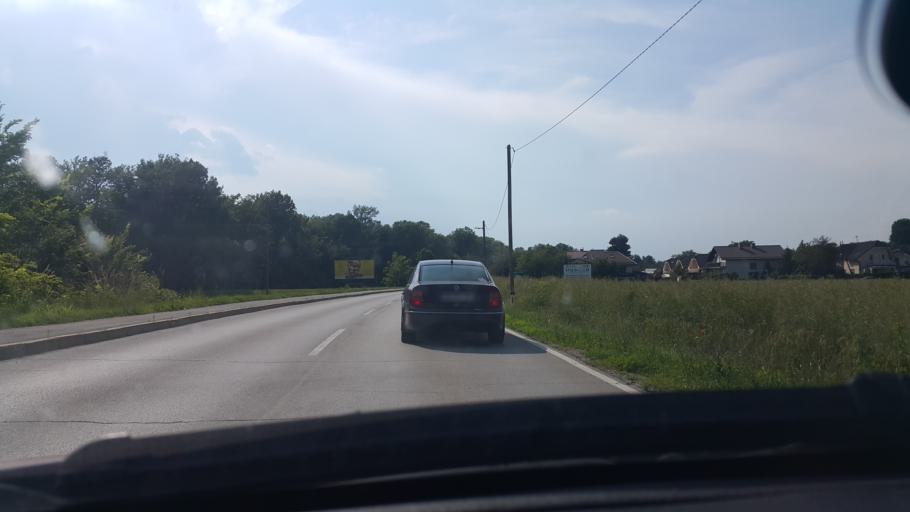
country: SI
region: Duplek
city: Zgornji Duplek
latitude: 46.5080
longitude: 15.7258
